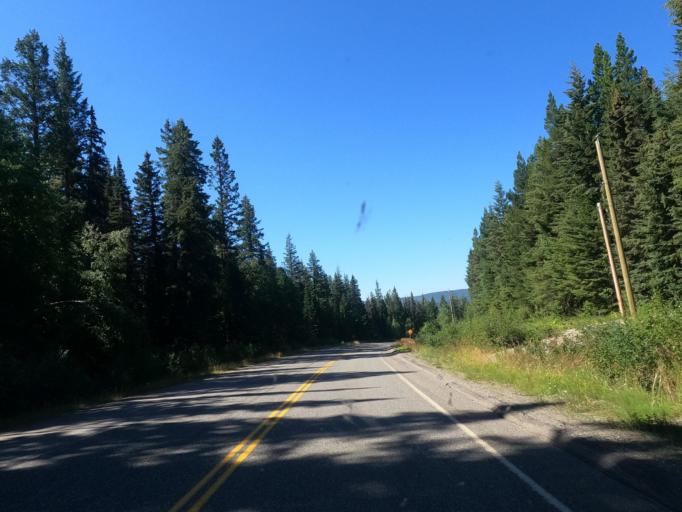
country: CA
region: British Columbia
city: Quesnel
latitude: 53.0238
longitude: -122.0574
